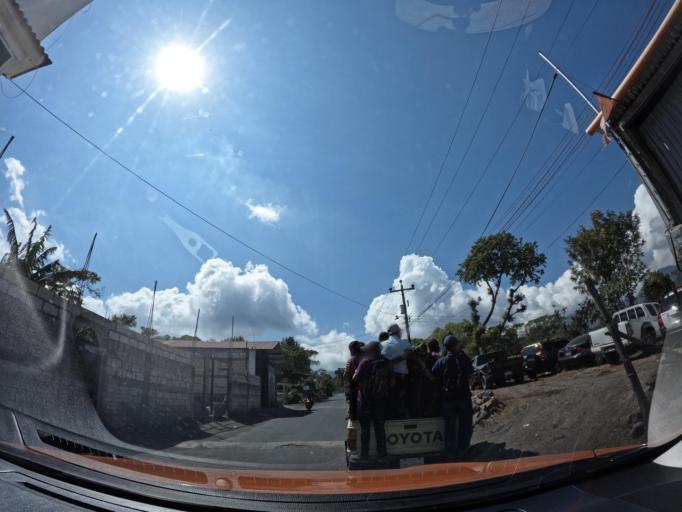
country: GT
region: Solola
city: Santiago Atitlan
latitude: 14.6263
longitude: -91.2327
